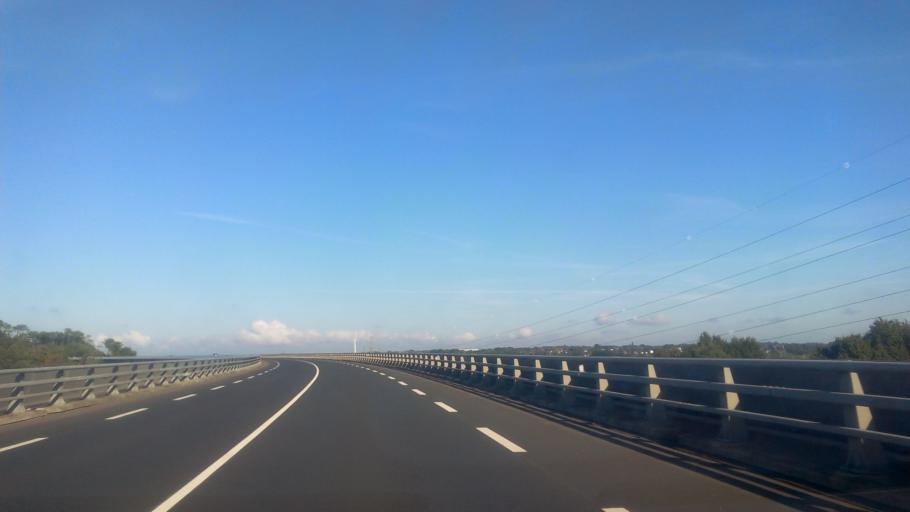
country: FR
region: Pays de la Loire
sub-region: Departement de la Loire-Atlantique
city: Saint-Nicolas-de-Redon
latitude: 47.6559
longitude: -2.0457
